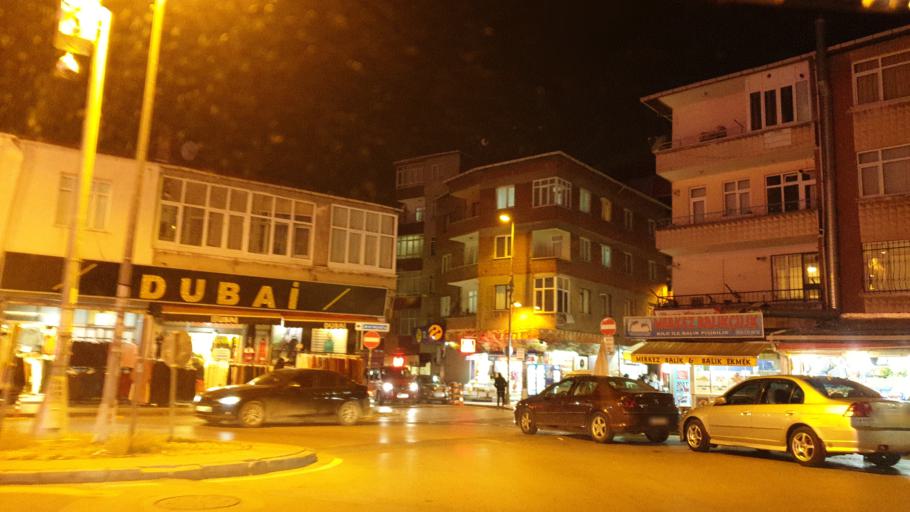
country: TR
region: Istanbul
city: Pendik
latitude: 40.8786
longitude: 29.2663
